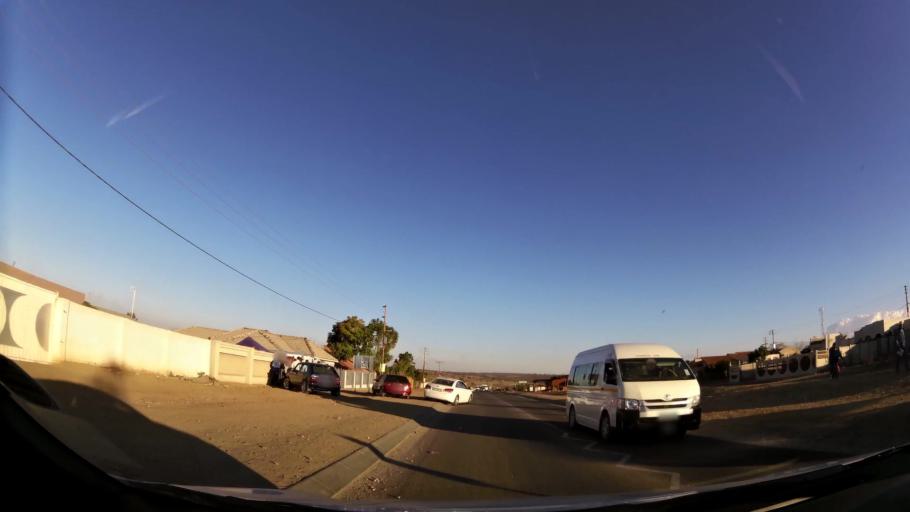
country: ZA
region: Limpopo
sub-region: Capricorn District Municipality
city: Polokwane
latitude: -23.8461
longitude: 29.3538
